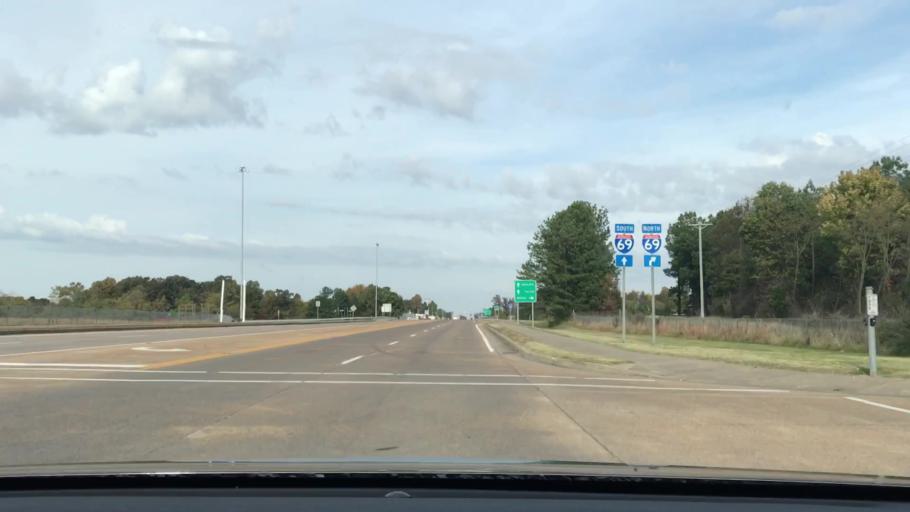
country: US
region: Kentucky
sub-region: Graves County
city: Mayfield
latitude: 36.7549
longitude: -88.6547
